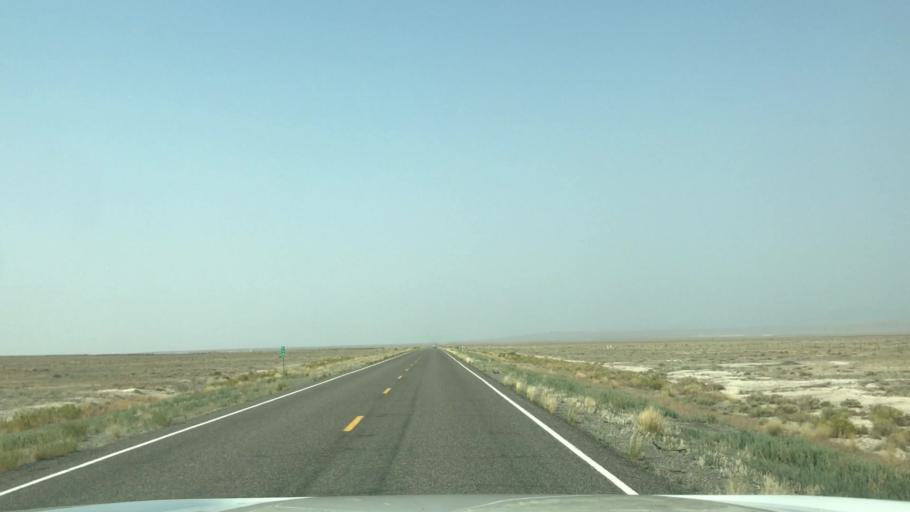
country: US
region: Utah
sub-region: Millard County
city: Delta
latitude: 39.2409
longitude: -112.9137
